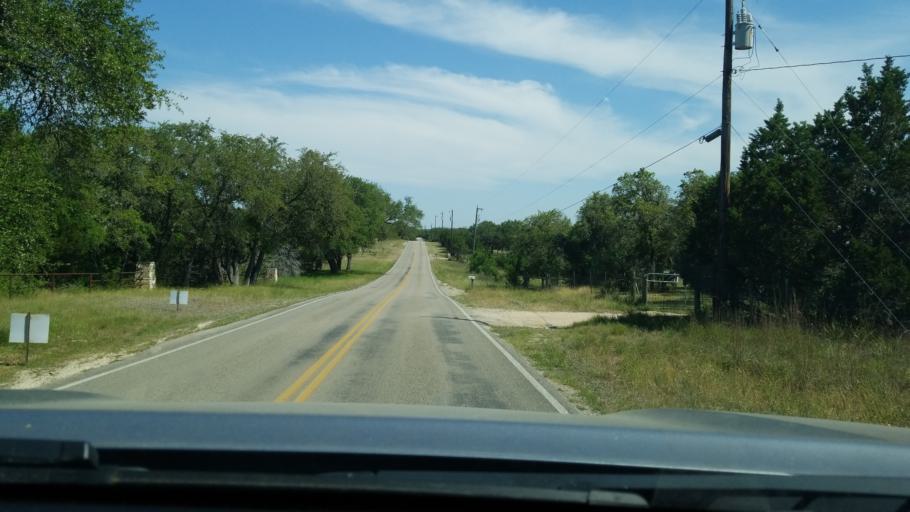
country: US
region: Texas
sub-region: Comal County
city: Bulverde
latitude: 29.7651
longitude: -98.5114
